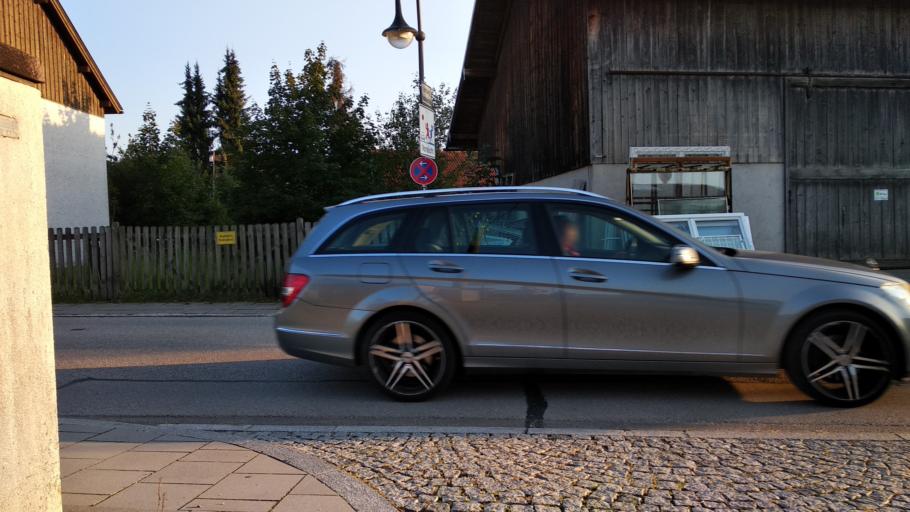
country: DE
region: Bavaria
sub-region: Upper Bavaria
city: Grasbrunn
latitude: 48.0601
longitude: 11.7726
